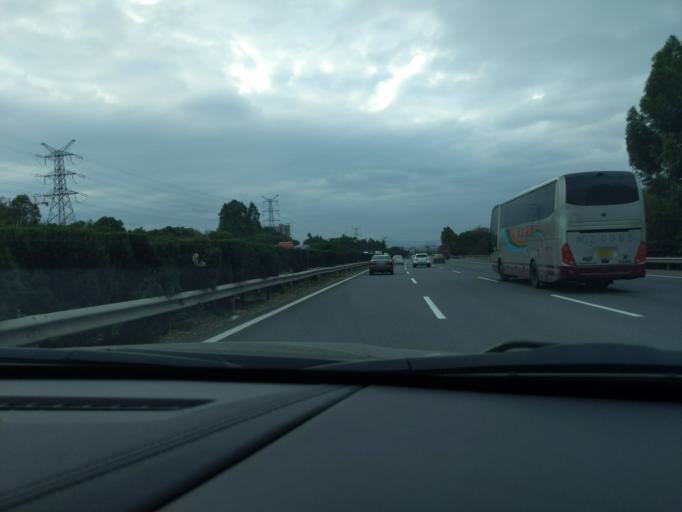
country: CN
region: Fujian
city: Hongtang
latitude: 24.6887
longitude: 118.2056
